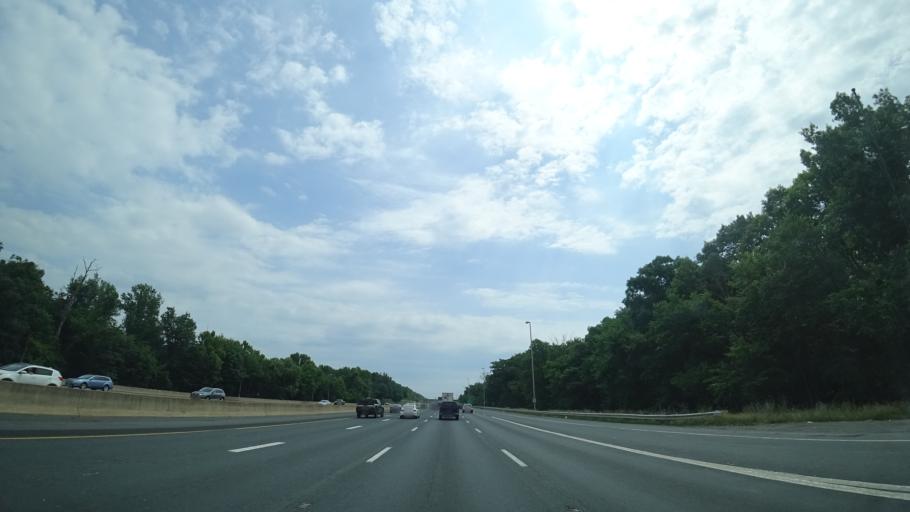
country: US
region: Virginia
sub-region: Prince William County
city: Sudley
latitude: 38.8089
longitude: -77.4929
